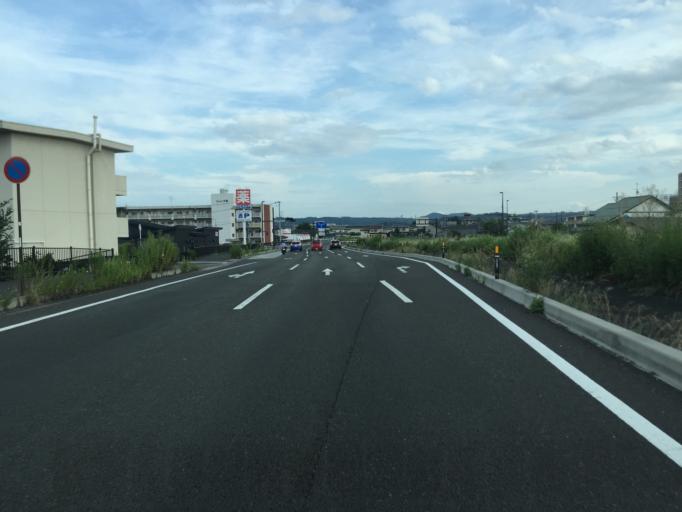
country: JP
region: Fukushima
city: Fukushima-shi
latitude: 37.7322
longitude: 140.4422
